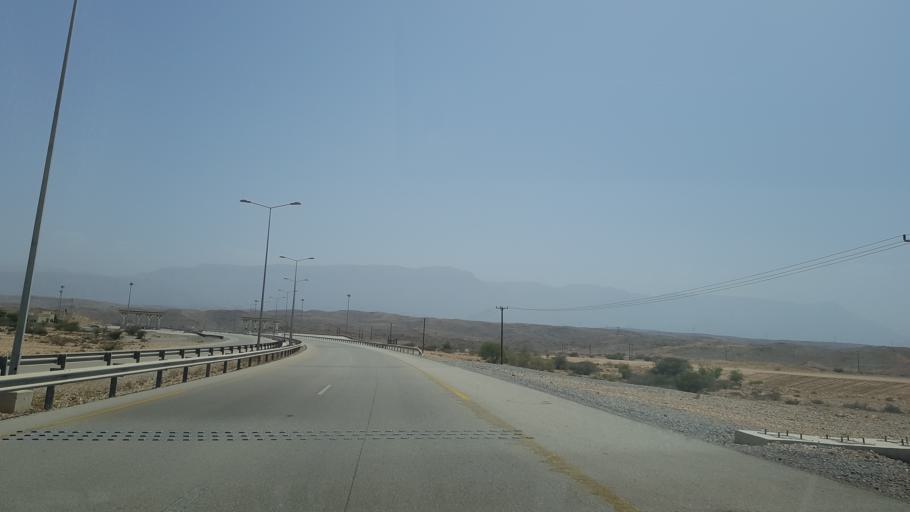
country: OM
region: Muhafazat Masqat
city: Muscat
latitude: 23.1530
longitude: 58.9692
